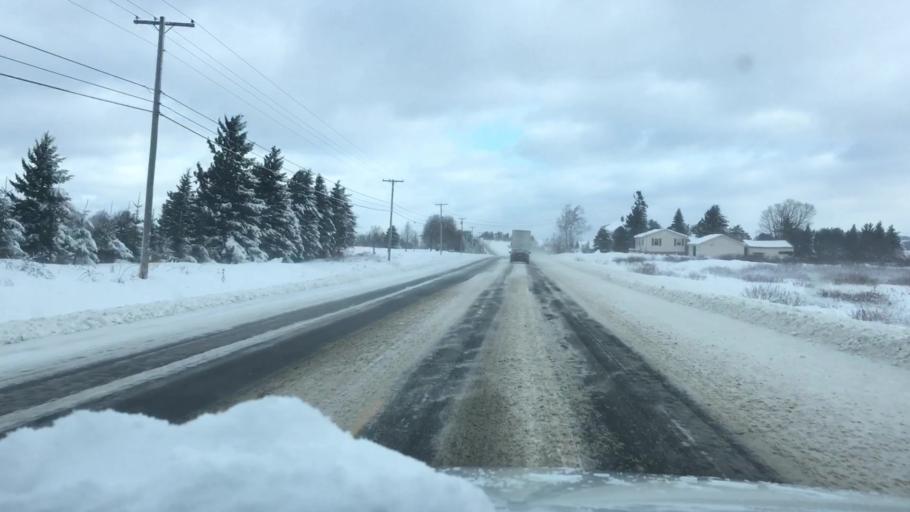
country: US
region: Maine
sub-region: Aroostook County
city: Presque Isle
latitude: 46.7397
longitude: -67.9977
